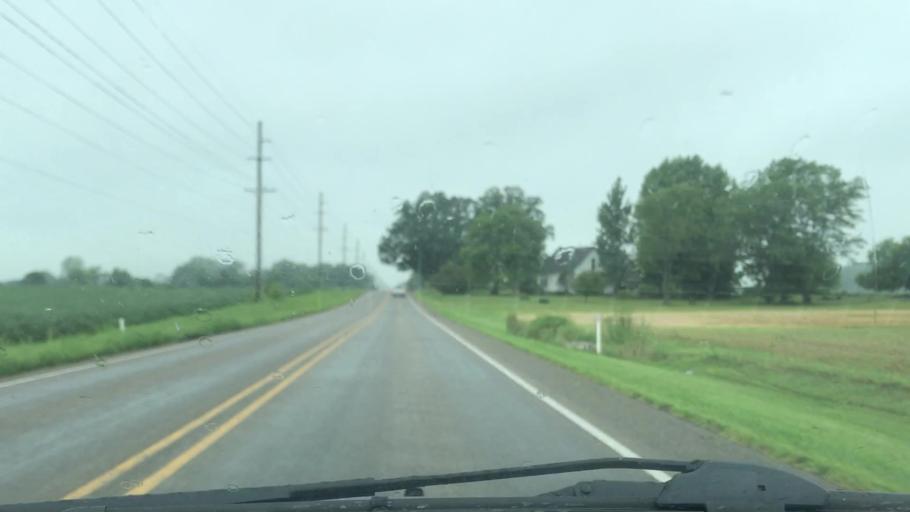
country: US
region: Indiana
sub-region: Hamilton County
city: Westfield
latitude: 40.1028
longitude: -86.1475
